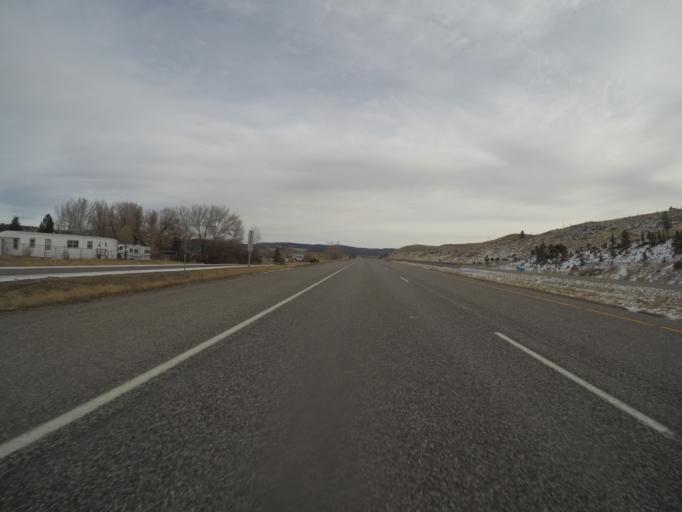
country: US
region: Montana
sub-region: Stillwater County
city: Absarokee
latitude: 45.7048
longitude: -109.5445
